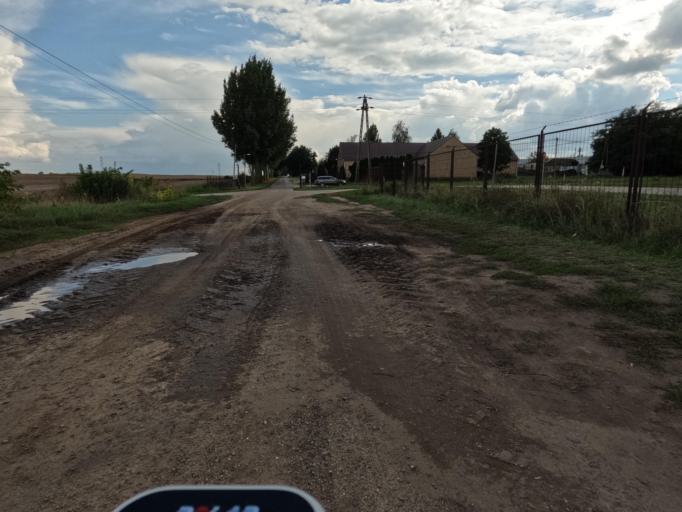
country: HU
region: Tolna
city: Tengelic
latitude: 46.5209
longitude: 18.7058
